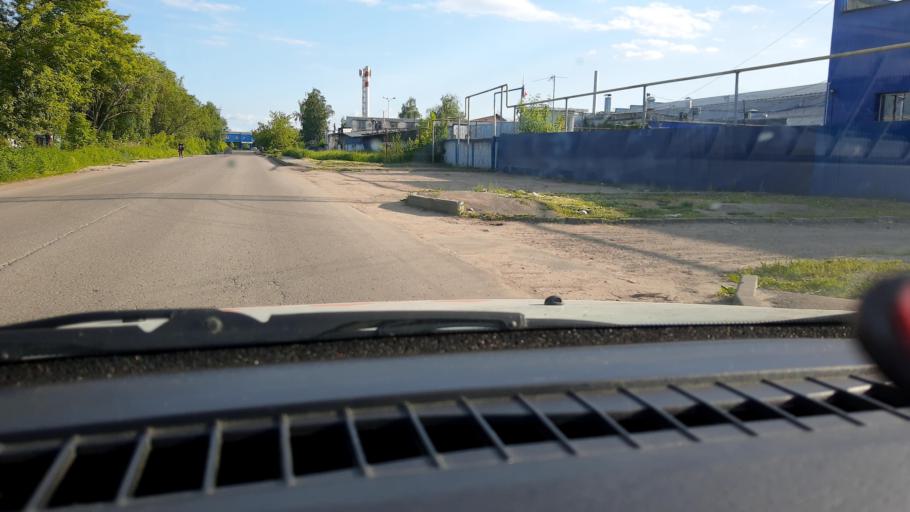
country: RU
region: Nizjnij Novgorod
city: Gorbatovka
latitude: 56.2500
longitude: 43.8073
